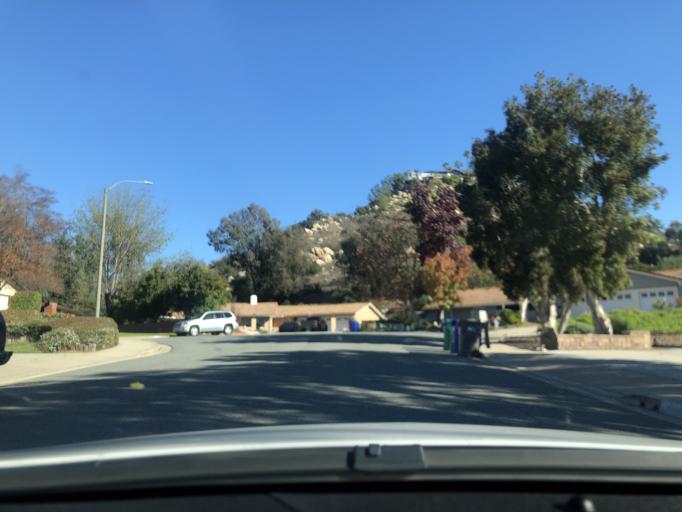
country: US
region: California
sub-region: San Diego County
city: El Cajon
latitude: 32.7801
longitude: -116.9438
